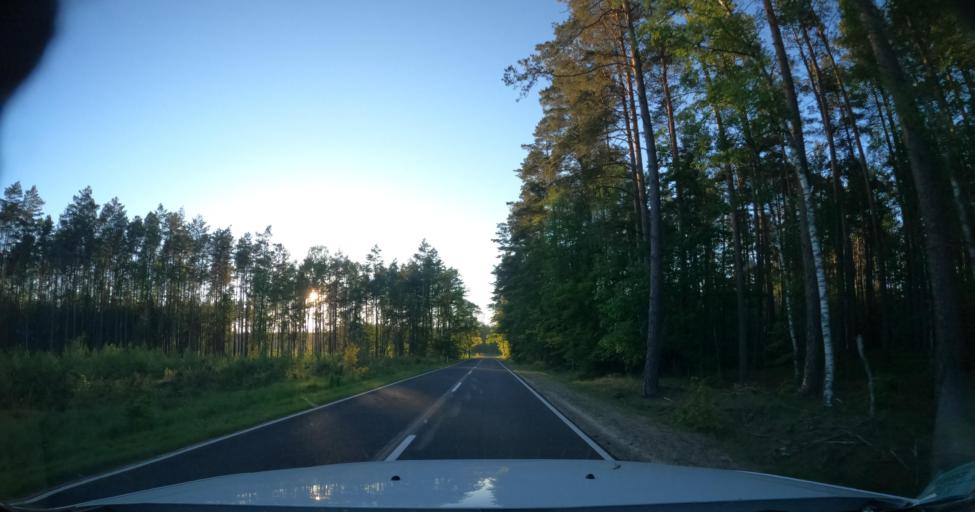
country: PL
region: Pomeranian Voivodeship
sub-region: Powiat slupski
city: Potegowo
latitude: 54.3901
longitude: 17.4756
